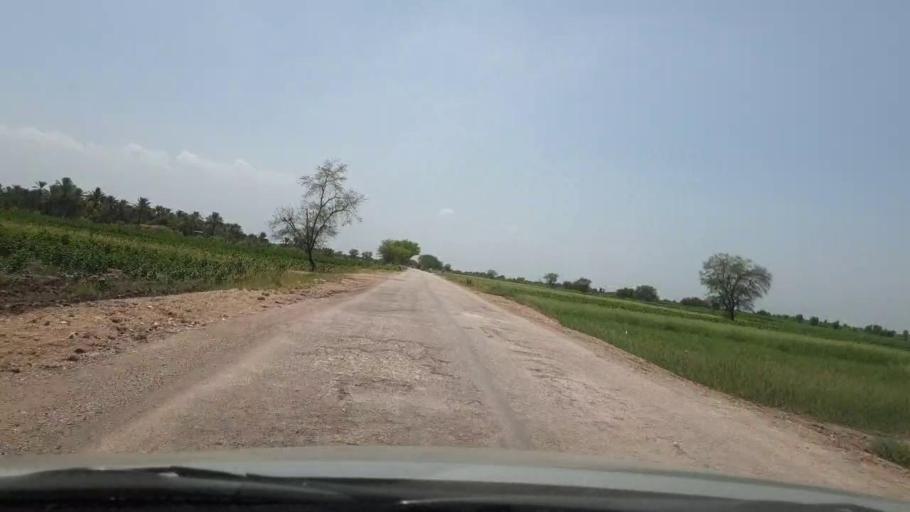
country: PK
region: Sindh
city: Pano Aqil
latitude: 27.6635
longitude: 69.1281
